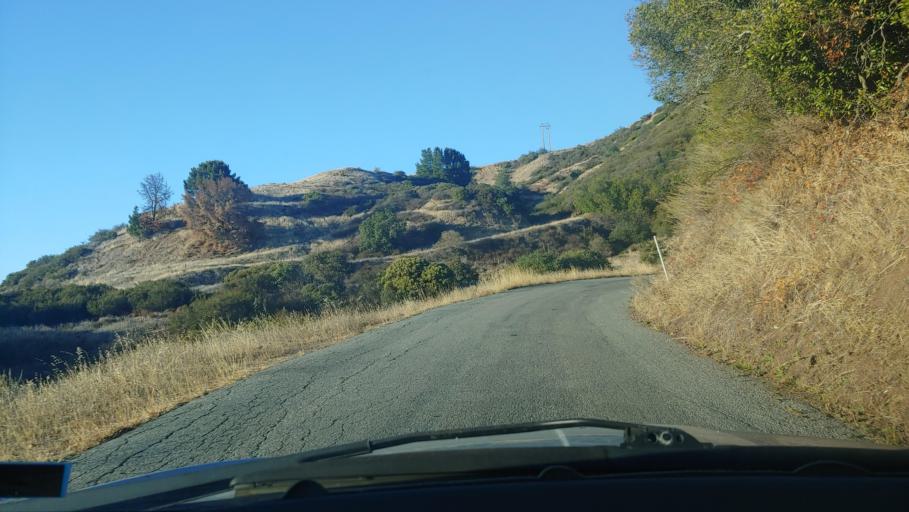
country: US
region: California
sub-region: Santa Barbara County
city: Goleta
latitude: 34.5143
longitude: -119.7963
